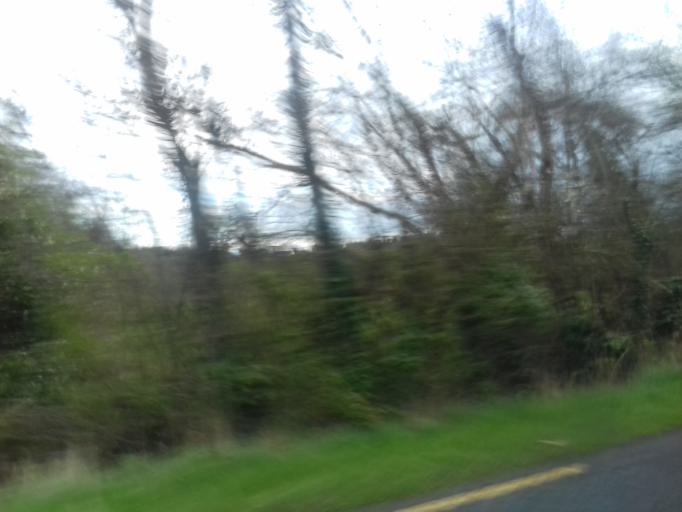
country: IE
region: Ulster
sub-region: An Cabhan
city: Ballyconnell
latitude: 54.0859
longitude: -7.5262
